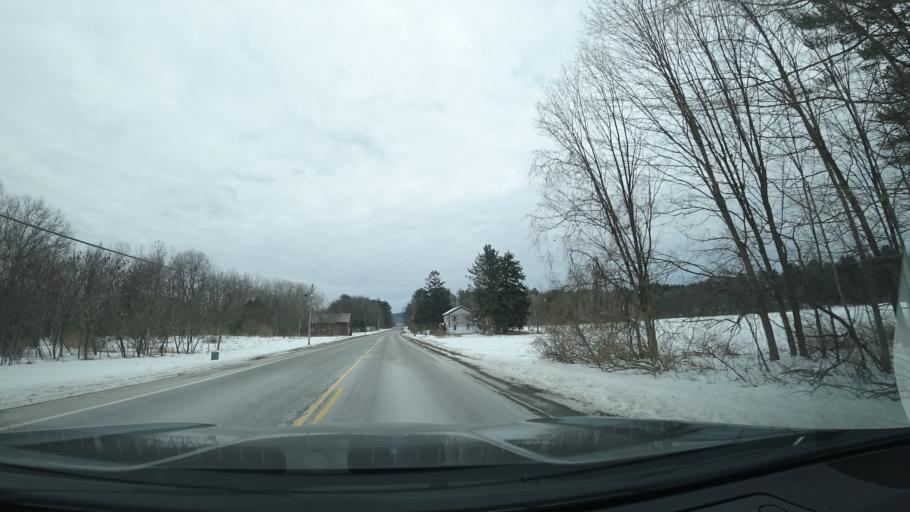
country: US
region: New York
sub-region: Washington County
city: Cambridge
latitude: 43.1504
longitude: -73.3666
